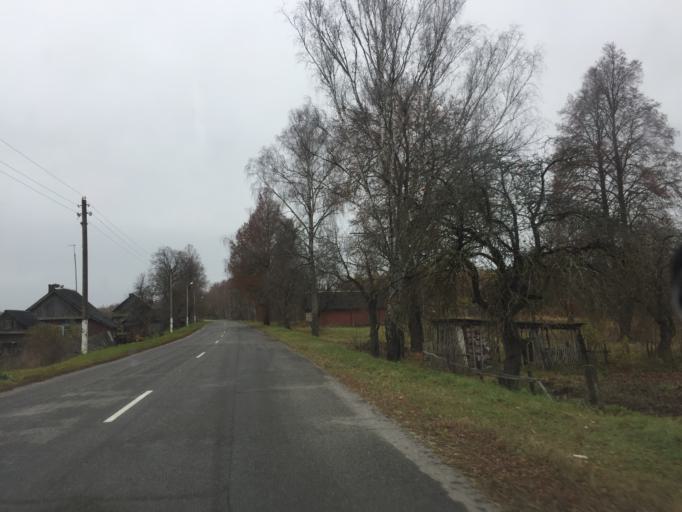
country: BY
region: Mogilev
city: Chavusy
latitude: 53.8789
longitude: 31.0511
